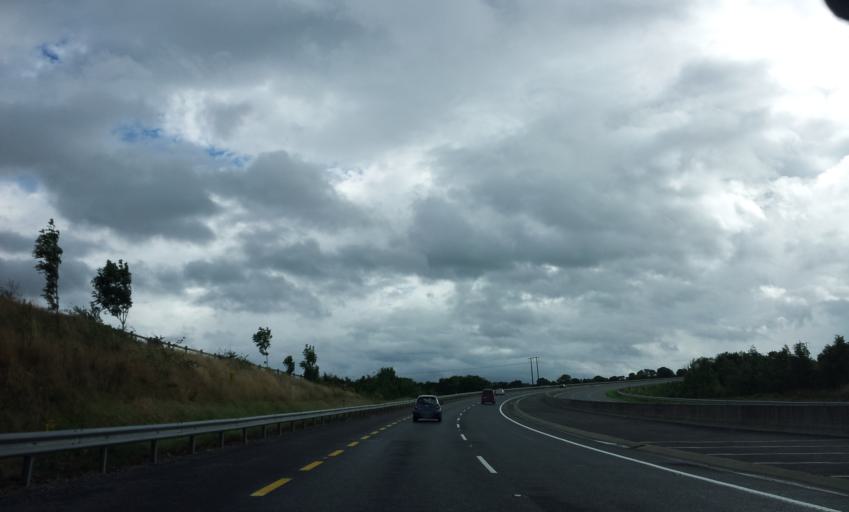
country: IE
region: Leinster
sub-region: Kilkenny
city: Mooncoin
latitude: 52.2424
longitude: -7.1892
